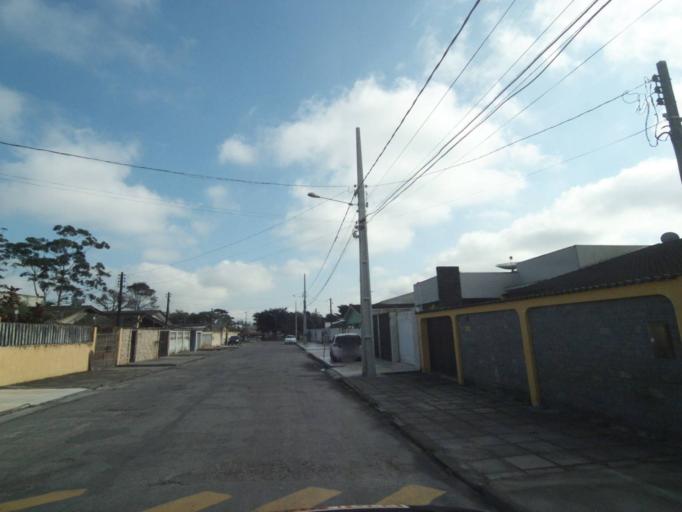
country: BR
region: Parana
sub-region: Paranagua
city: Paranagua
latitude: -25.5572
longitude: -48.5602
